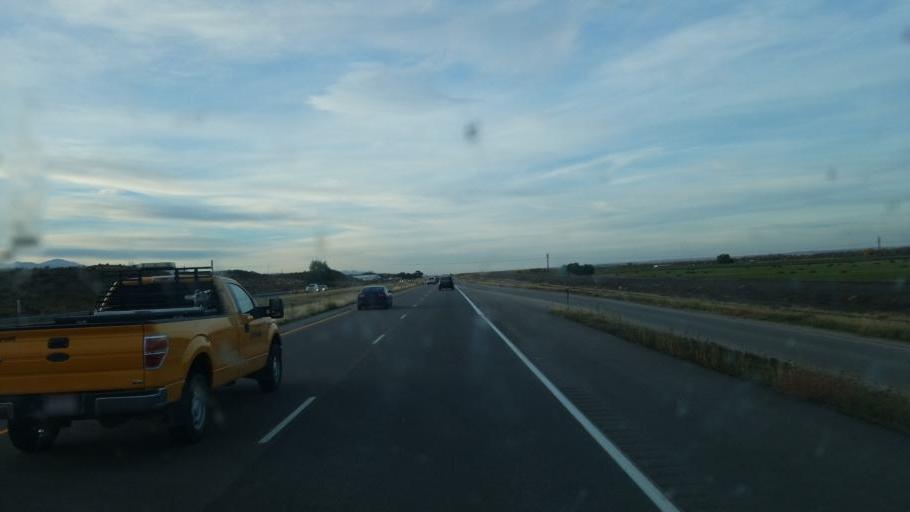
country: US
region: Colorado
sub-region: El Paso County
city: Fountain
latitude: 38.5539
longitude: -104.6481
